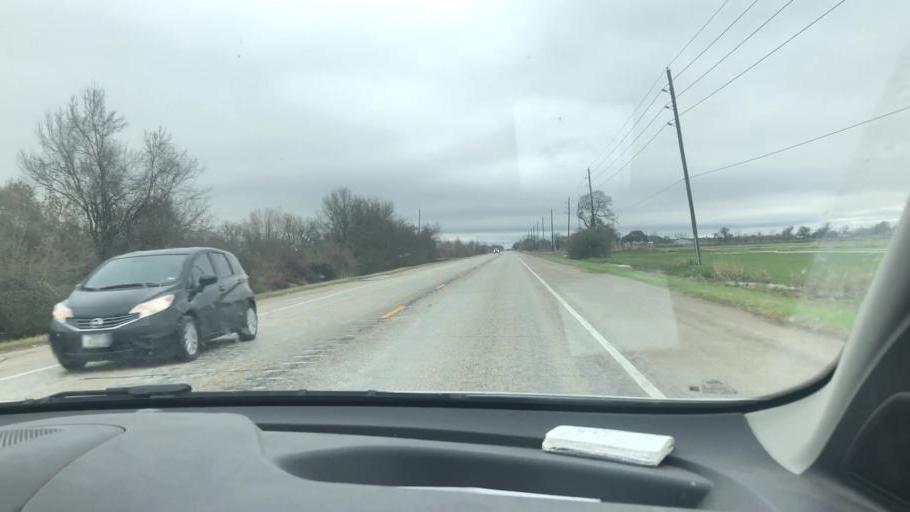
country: US
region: Texas
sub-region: Wharton County
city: Wharton
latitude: 29.2736
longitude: -96.0620
